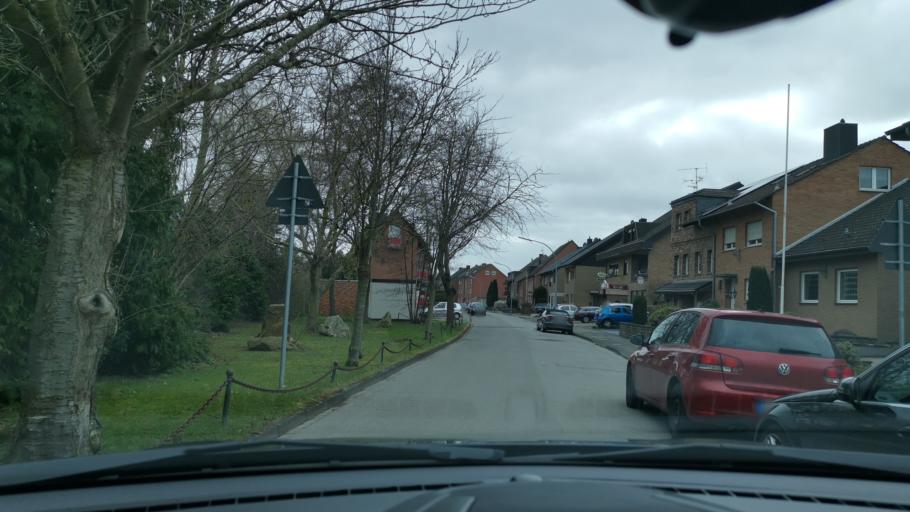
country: DE
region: North Rhine-Westphalia
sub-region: Regierungsbezirk Dusseldorf
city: Grevenbroich
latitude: 51.0756
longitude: 6.5717
